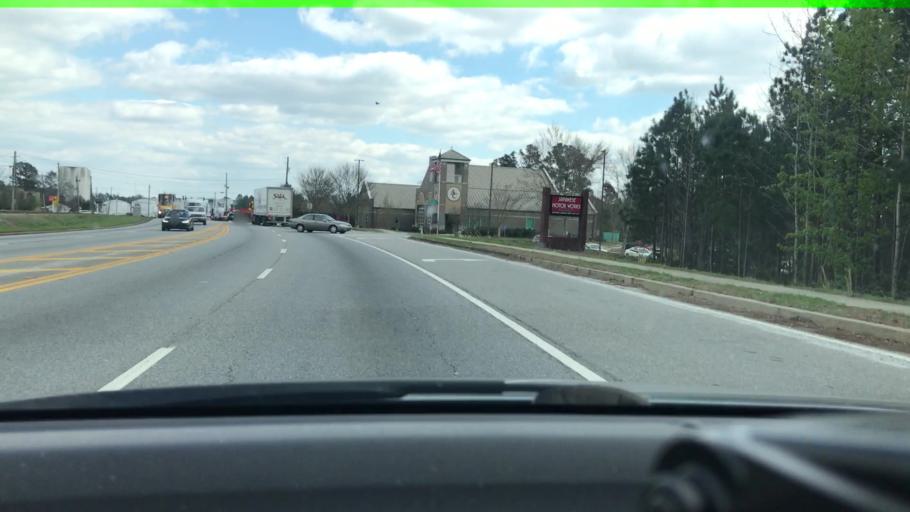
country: US
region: Georgia
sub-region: Clarke County
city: Country Club Estates
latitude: 33.9895
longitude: -83.4286
